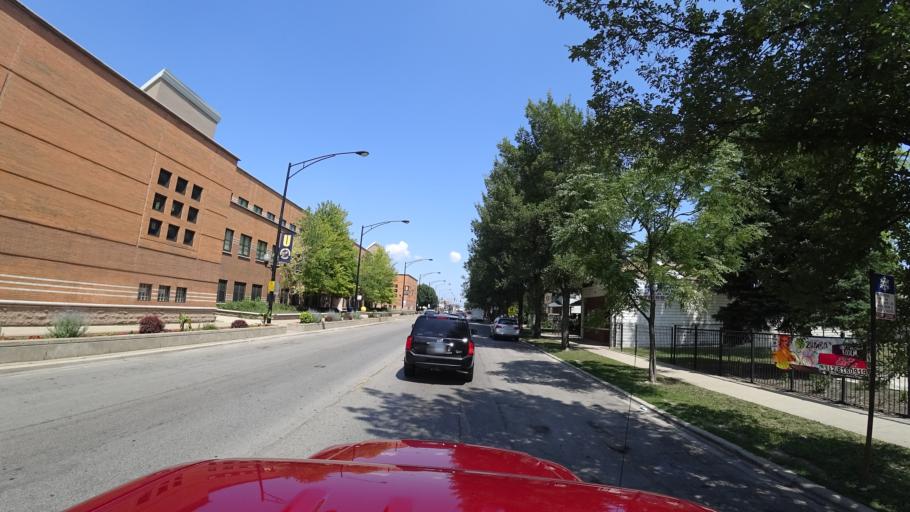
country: US
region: Illinois
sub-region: Cook County
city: Cicero
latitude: 41.8104
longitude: -87.7041
